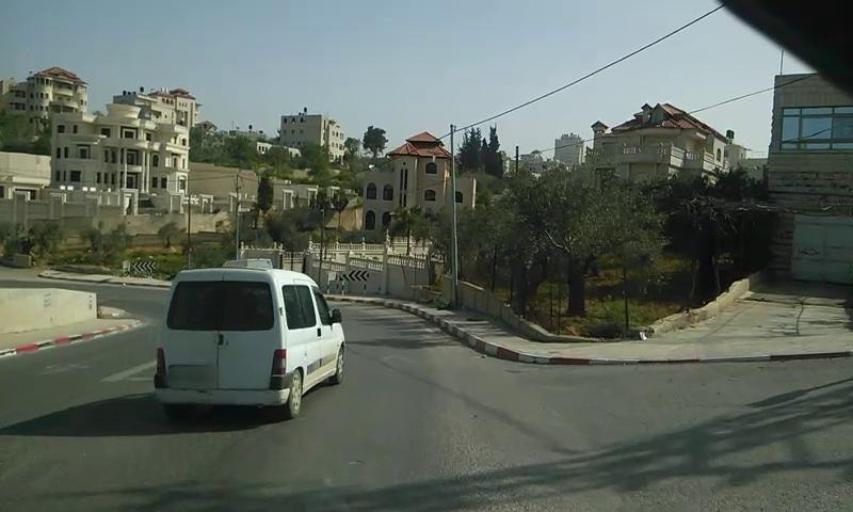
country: PS
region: West Bank
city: Dura al Qar`
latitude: 31.9582
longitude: 35.2251
